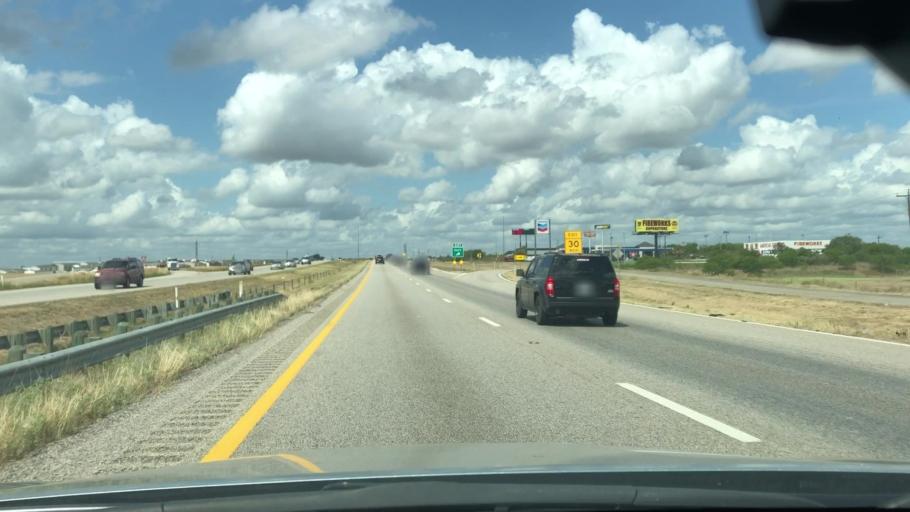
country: US
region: Texas
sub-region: Guadalupe County
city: McQueeney
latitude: 29.5416
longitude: -98.0689
